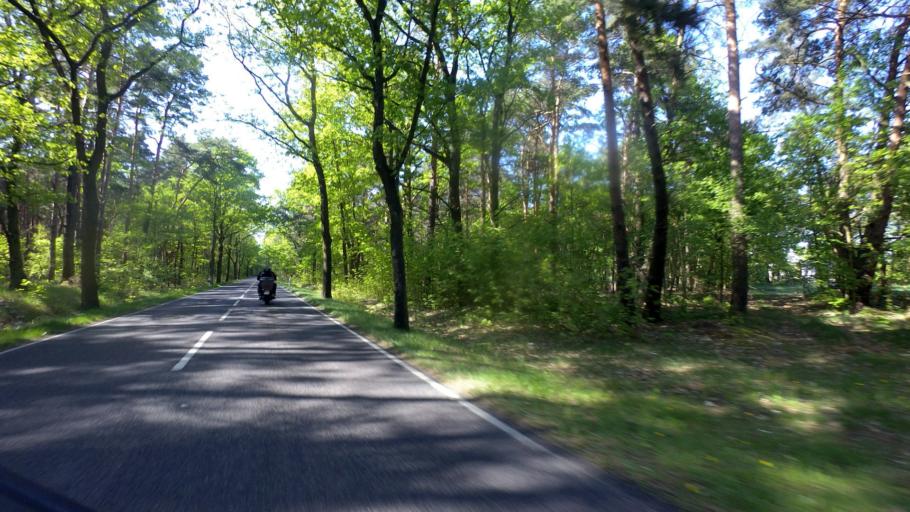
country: DE
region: Brandenburg
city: Bestensee
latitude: 52.2268
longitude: 13.6736
